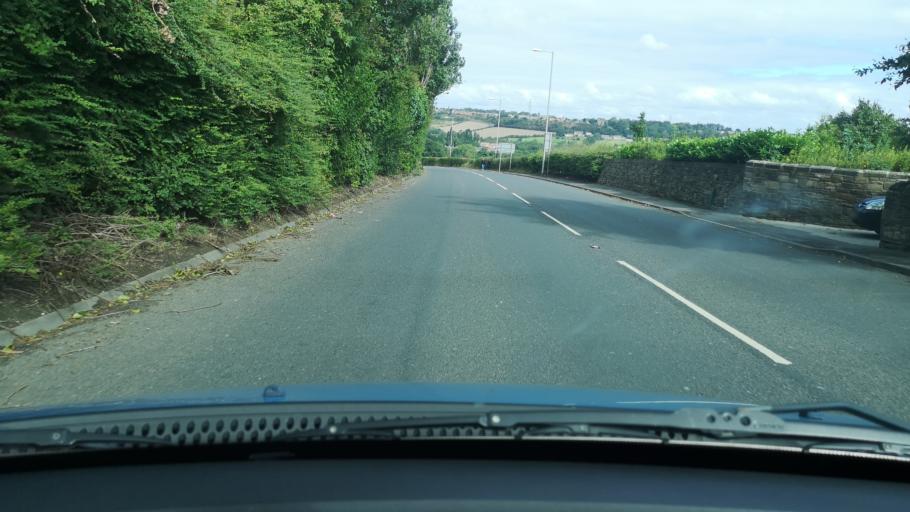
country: GB
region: England
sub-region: City and Borough of Wakefield
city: Horbury
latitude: 53.6506
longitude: -1.5740
